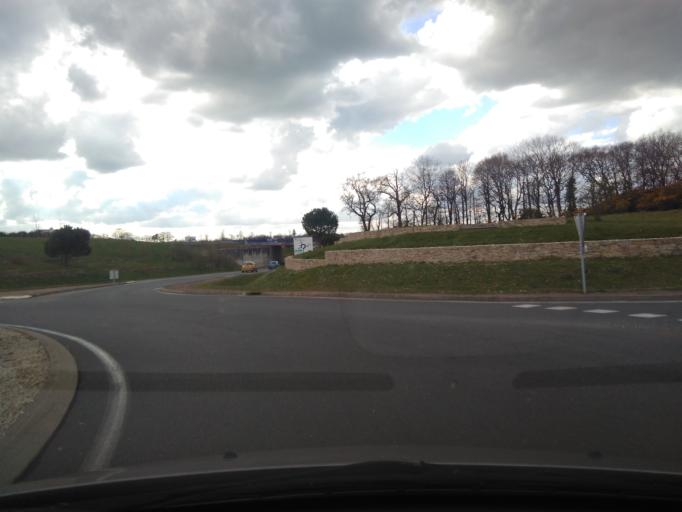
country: FR
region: Pays de la Loire
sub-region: Departement de la Vendee
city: La Verrie
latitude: 46.9469
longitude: -0.9799
